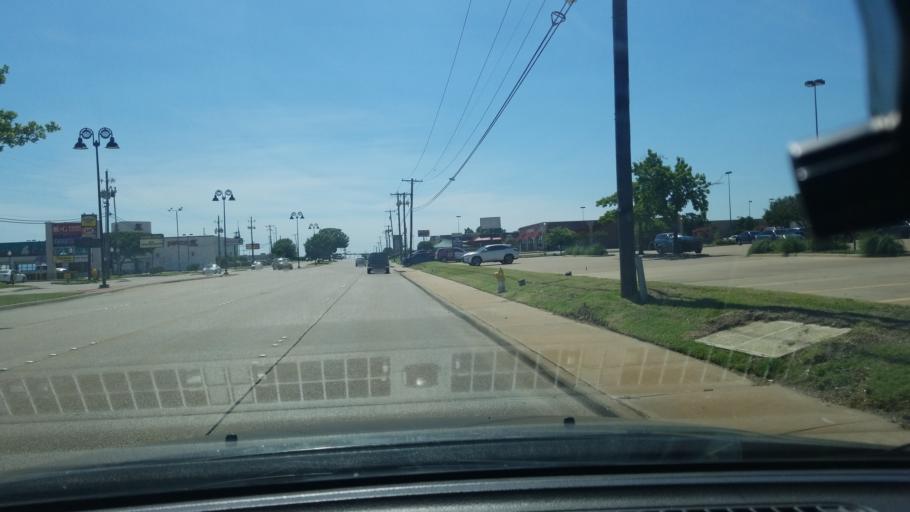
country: US
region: Texas
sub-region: Dallas County
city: Mesquite
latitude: 32.8109
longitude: -96.6176
